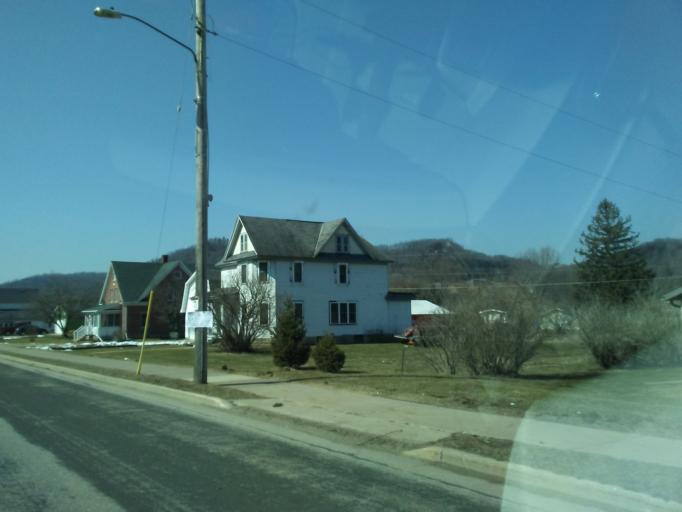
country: US
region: Wisconsin
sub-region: Vernon County
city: Westby
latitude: 43.7024
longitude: -91.0128
